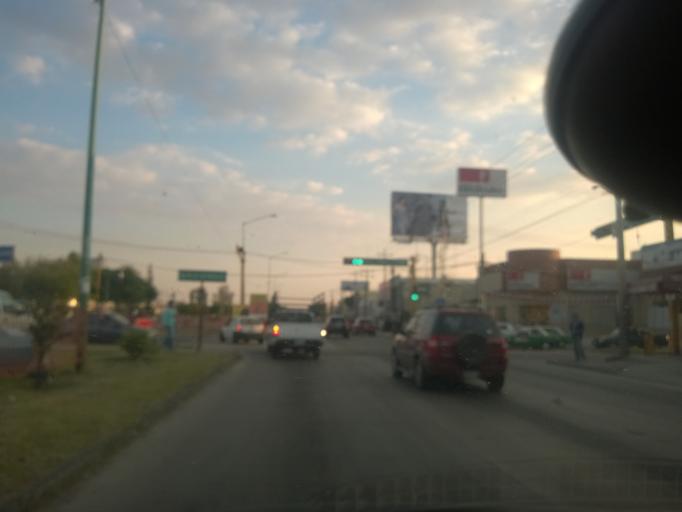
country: MX
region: Guanajuato
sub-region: Leon
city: Medina
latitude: 21.1480
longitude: -101.6346
